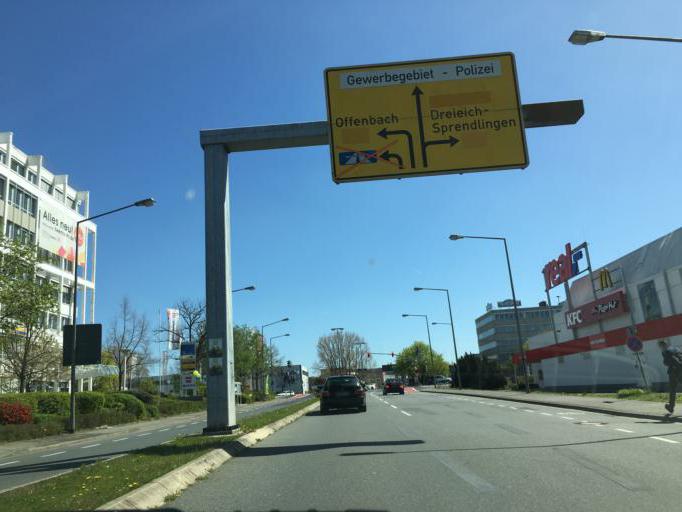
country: DE
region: Hesse
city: Dreieich
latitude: 50.0320
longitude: 8.7040
